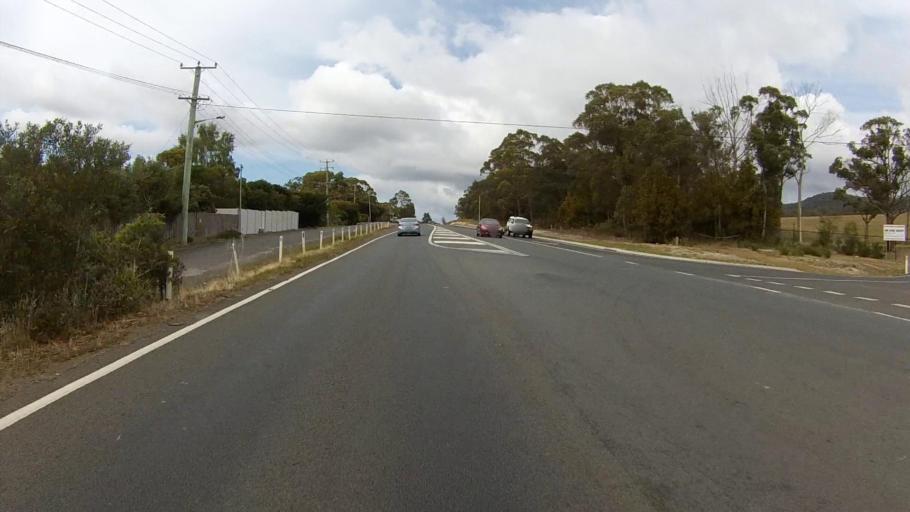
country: AU
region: Tasmania
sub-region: Kingborough
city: Margate
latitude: -43.0434
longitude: 147.2662
